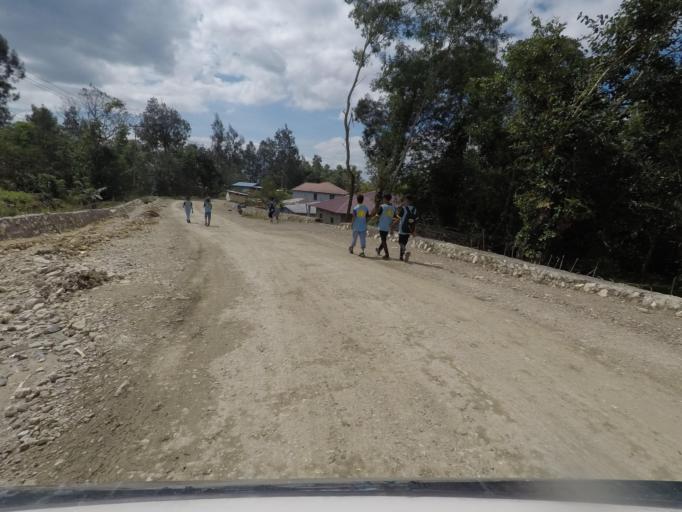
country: TL
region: Baucau
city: Venilale
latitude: -8.7392
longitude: 126.3773
